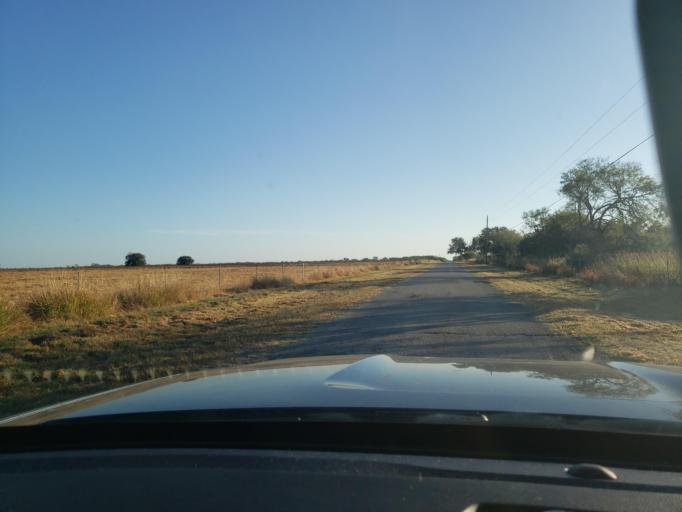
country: US
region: Texas
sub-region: Bee County
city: Beeville
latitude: 28.4298
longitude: -97.6920
